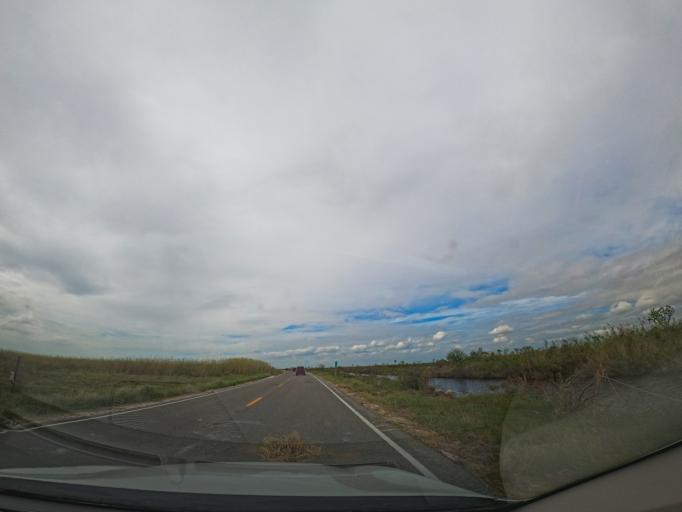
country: US
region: Louisiana
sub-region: Cameron Parish
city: Cameron
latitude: 29.7715
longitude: -93.4362
